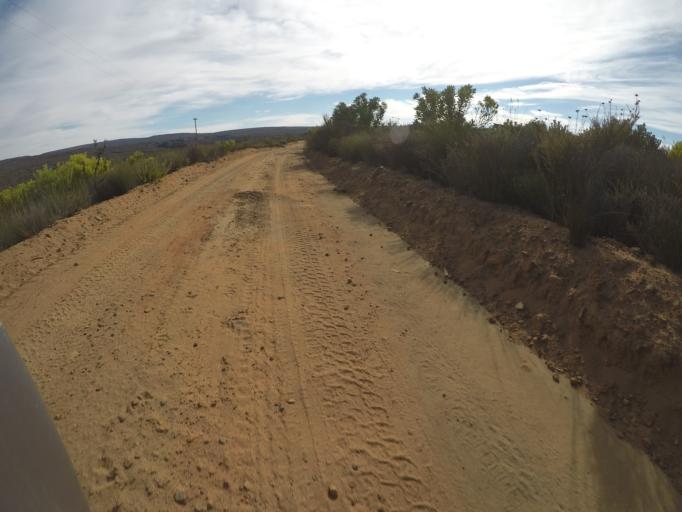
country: ZA
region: Western Cape
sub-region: West Coast District Municipality
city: Vredendal
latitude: -31.7489
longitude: 18.8230
